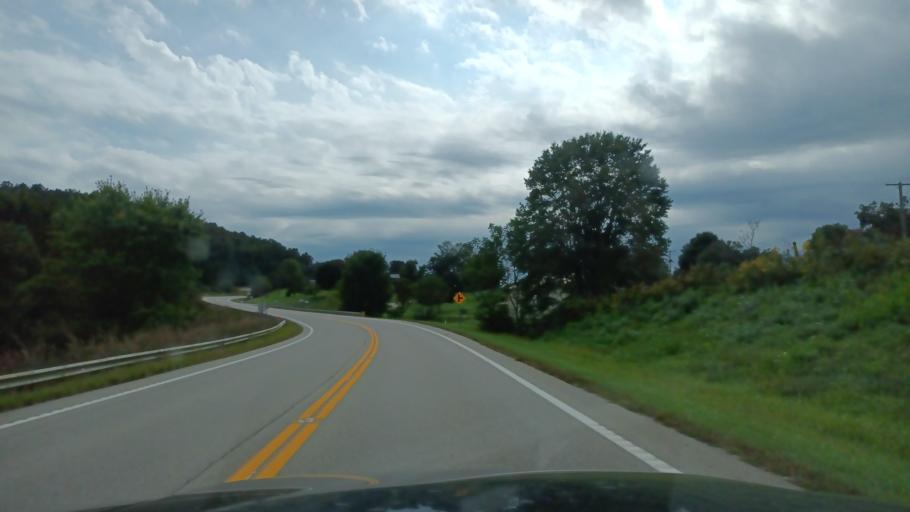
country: US
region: Ohio
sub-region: Vinton County
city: McArthur
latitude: 39.2647
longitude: -82.6810
